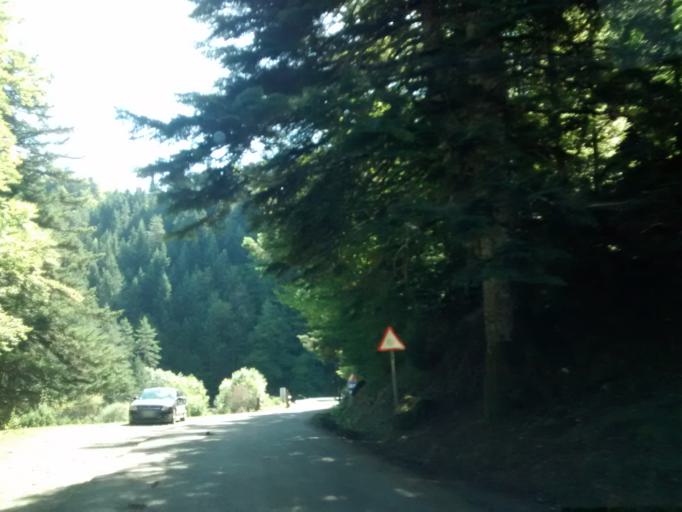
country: ES
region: Aragon
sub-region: Provincia de Huesca
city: Aragues del Puerto
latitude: 42.8302
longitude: -0.7121
